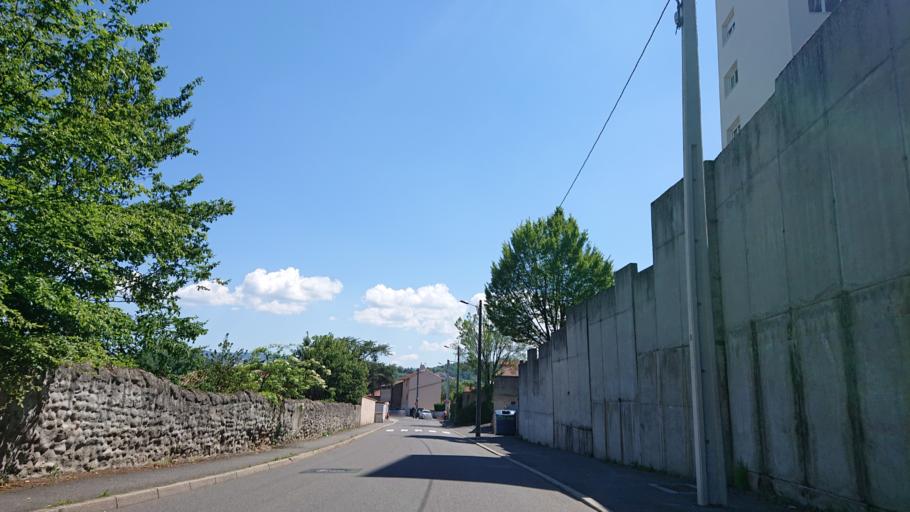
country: FR
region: Rhone-Alpes
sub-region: Departement de la Loire
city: Villars
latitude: 45.4482
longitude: 4.3606
